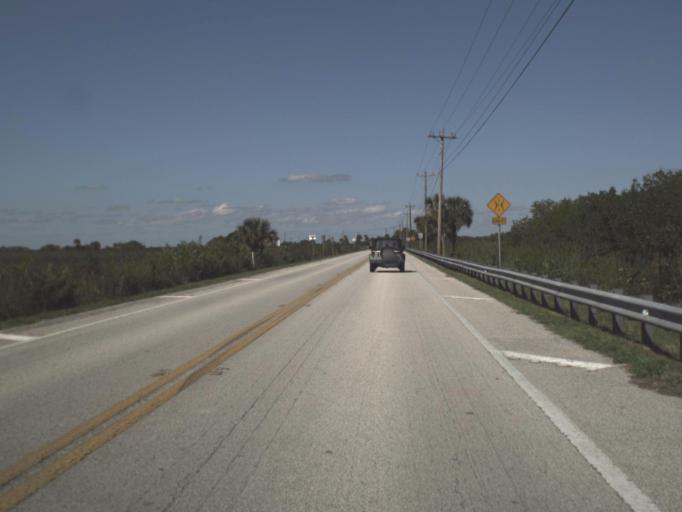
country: US
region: Florida
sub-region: Collier County
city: Marco
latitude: 25.9146
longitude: -81.3734
